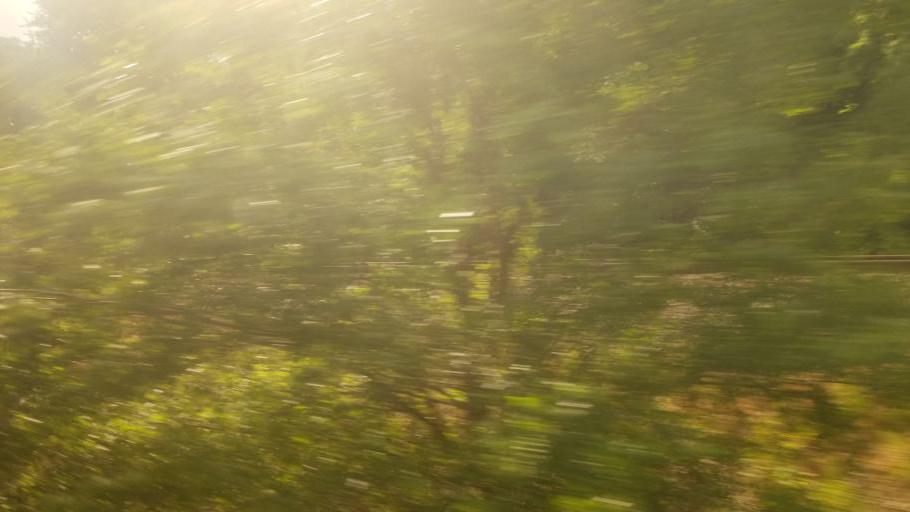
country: US
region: Kansas
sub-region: Wyandotte County
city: Edwardsville
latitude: 39.0469
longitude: -94.7802
